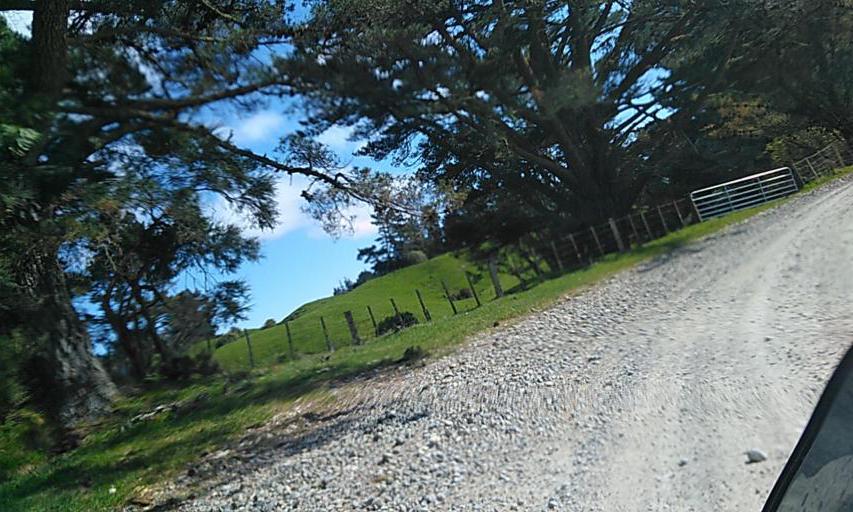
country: NZ
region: Gisborne
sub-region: Gisborne District
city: Gisborne
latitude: -38.2051
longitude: 178.0616
